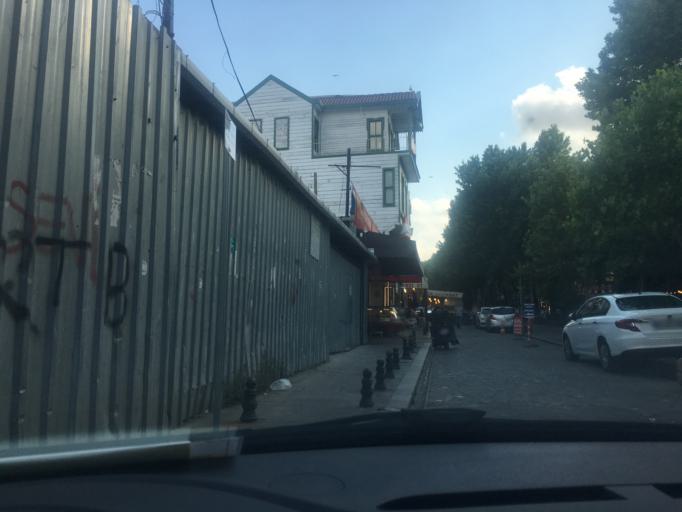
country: TR
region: Istanbul
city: Istanbul
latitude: 41.0181
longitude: 28.9562
